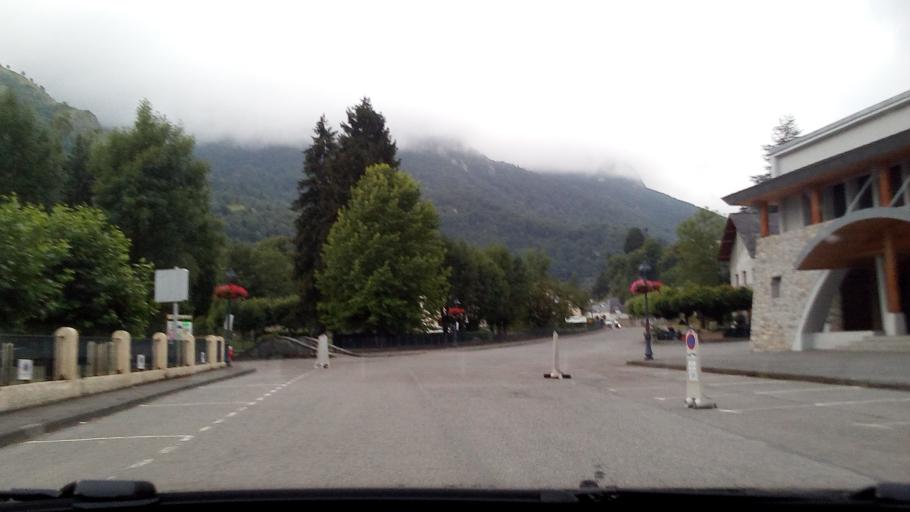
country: FR
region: Midi-Pyrenees
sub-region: Departement des Hautes-Pyrenees
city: Cauterets
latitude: 42.9550
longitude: -0.2140
